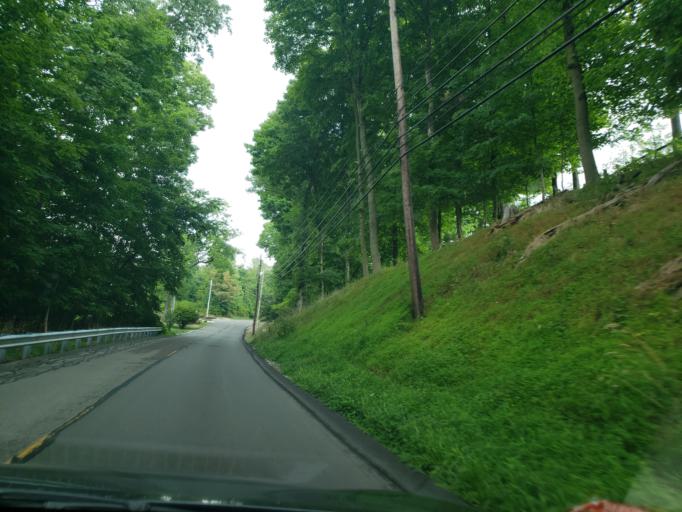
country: US
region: Pennsylvania
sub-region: Allegheny County
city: Coraopolis
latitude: 40.5307
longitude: -80.1499
